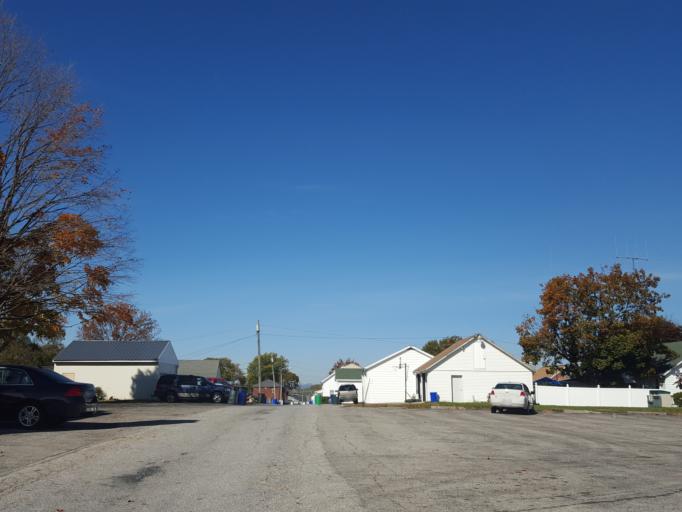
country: US
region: Pennsylvania
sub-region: York County
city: Dallastown
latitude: 39.9024
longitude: -76.6478
